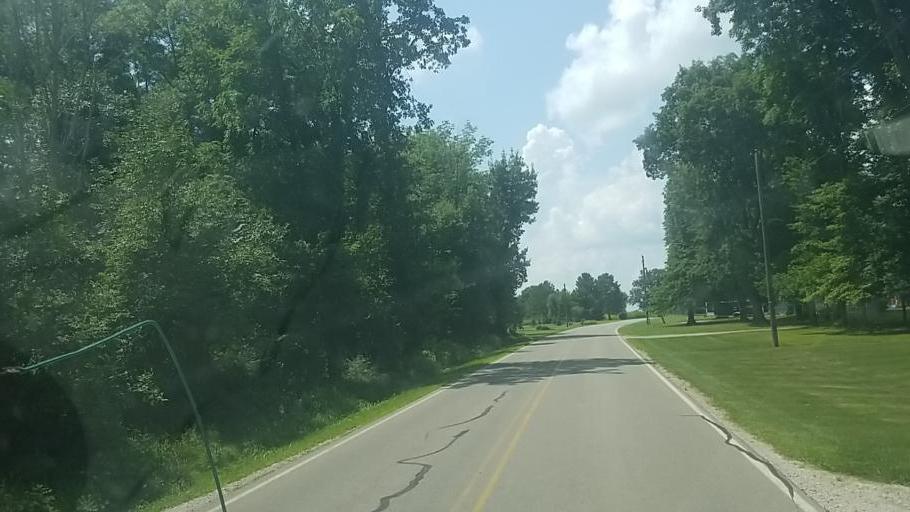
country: US
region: Ohio
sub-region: Crawford County
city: Bucyrus
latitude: 40.7707
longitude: -83.0347
